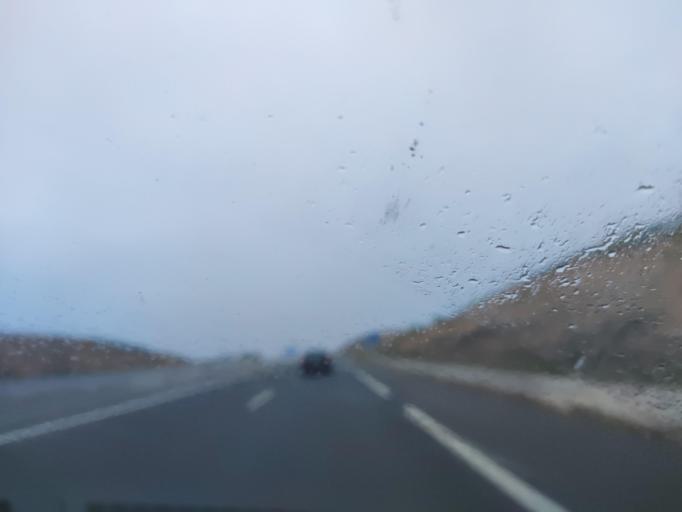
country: ES
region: Castille-La Mancha
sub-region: Province of Toledo
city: Bargas
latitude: 39.9093
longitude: -4.0597
